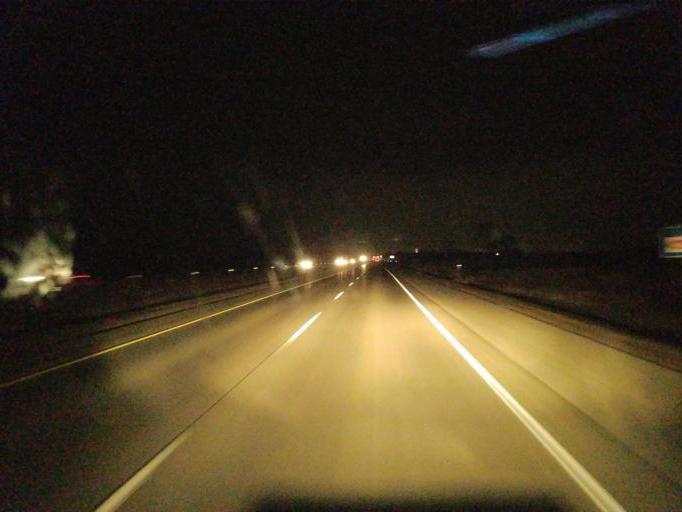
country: US
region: Iowa
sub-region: Dallas County
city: De Soto
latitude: 41.5291
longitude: -94.0489
